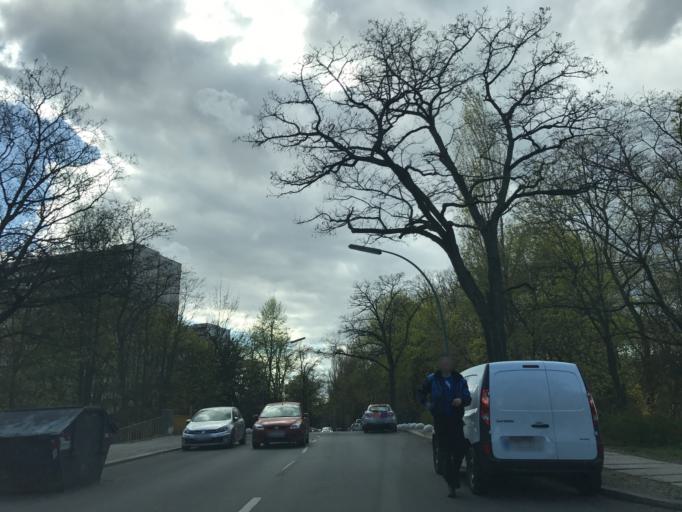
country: DE
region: Berlin
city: Tegel
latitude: 52.5776
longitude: 13.2754
